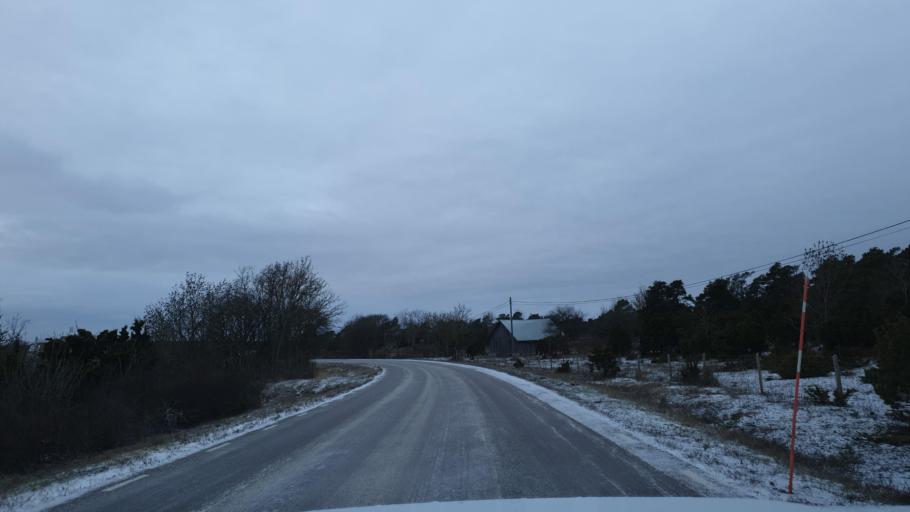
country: SE
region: Gotland
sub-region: Gotland
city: Slite
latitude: 57.4203
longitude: 18.8895
